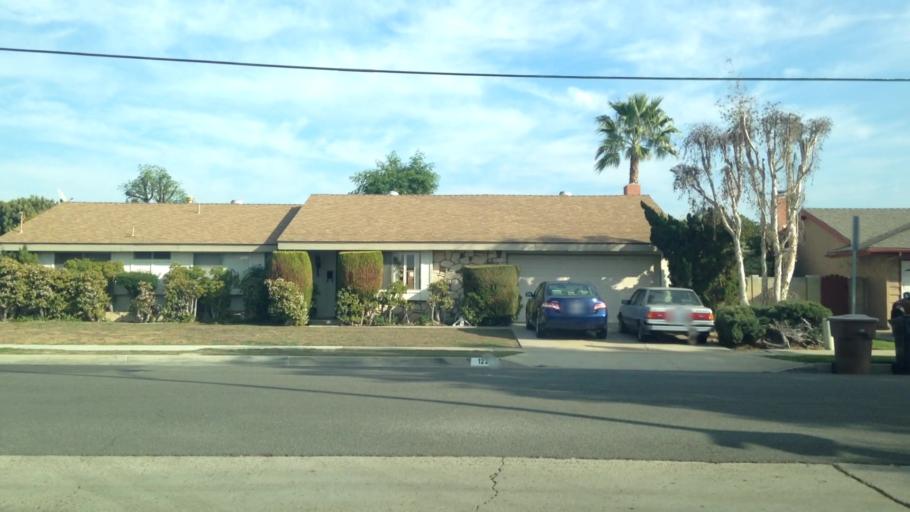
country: US
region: California
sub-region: Orange County
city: Yorba Linda
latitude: 33.8840
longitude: -117.8375
